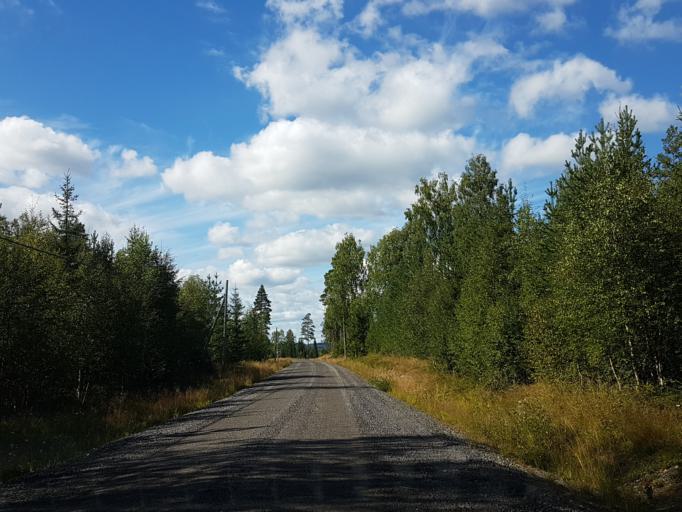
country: SE
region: Vaesterbotten
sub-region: Skelleftea Kommun
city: Burtraesk
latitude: 64.2820
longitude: 20.4669
